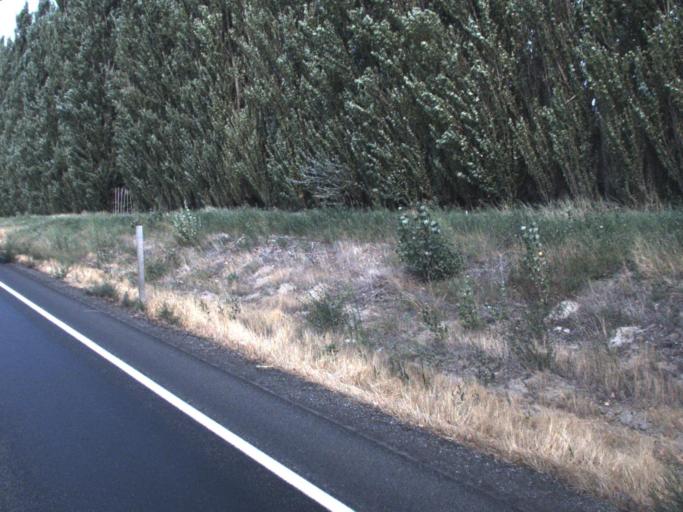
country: US
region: Oregon
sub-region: Morrow County
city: Irrigon
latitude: 45.9478
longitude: -119.6029
